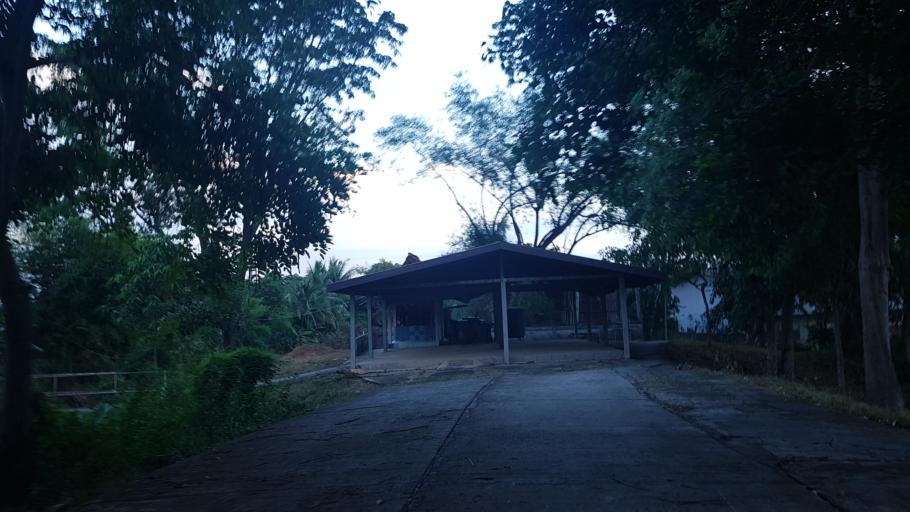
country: TH
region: Nakhon Ratchasima
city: Bua Lai
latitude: 15.6384
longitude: 102.5701
